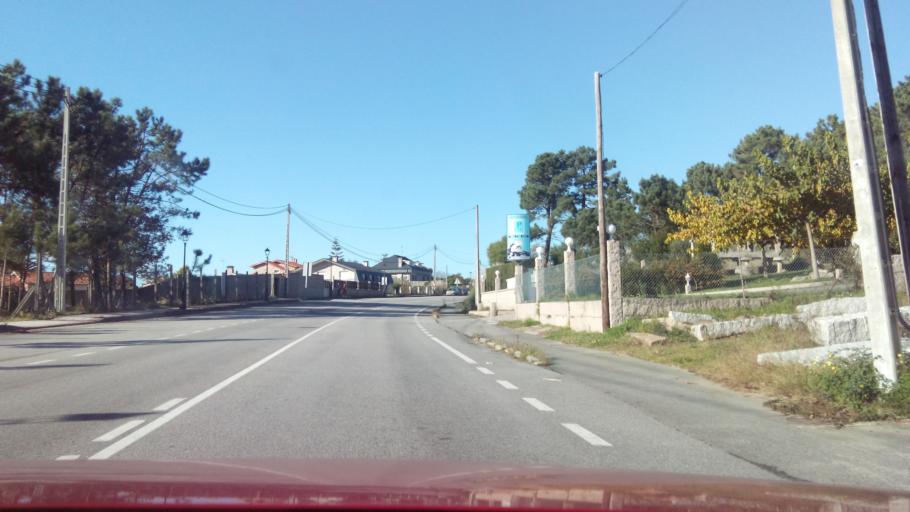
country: ES
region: Galicia
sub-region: Provincia de Pontevedra
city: O Grove
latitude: 42.4641
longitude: -8.9030
